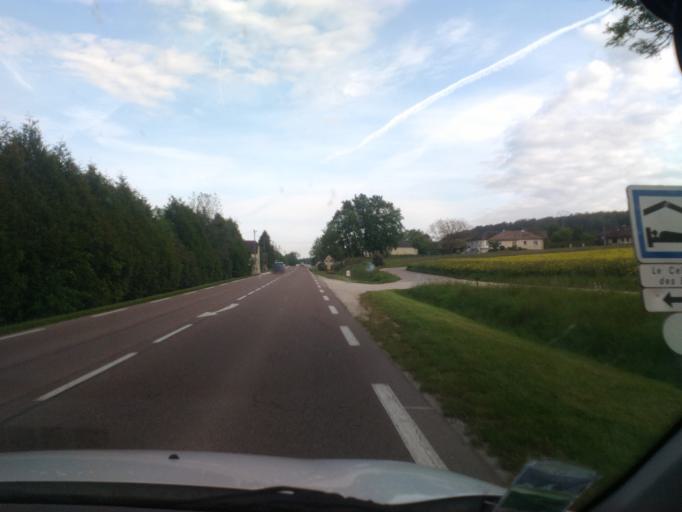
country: FR
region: Champagne-Ardenne
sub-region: Departement de l'Aube
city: Bar-sur-Aube
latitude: 48.2512
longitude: 4.6863
